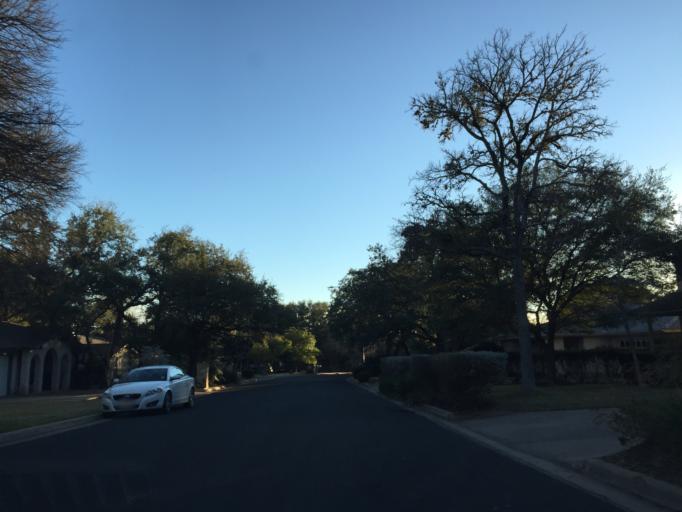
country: US
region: Texas
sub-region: Williamson County
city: Jollyville
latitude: 30.4234
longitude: -97.7616
